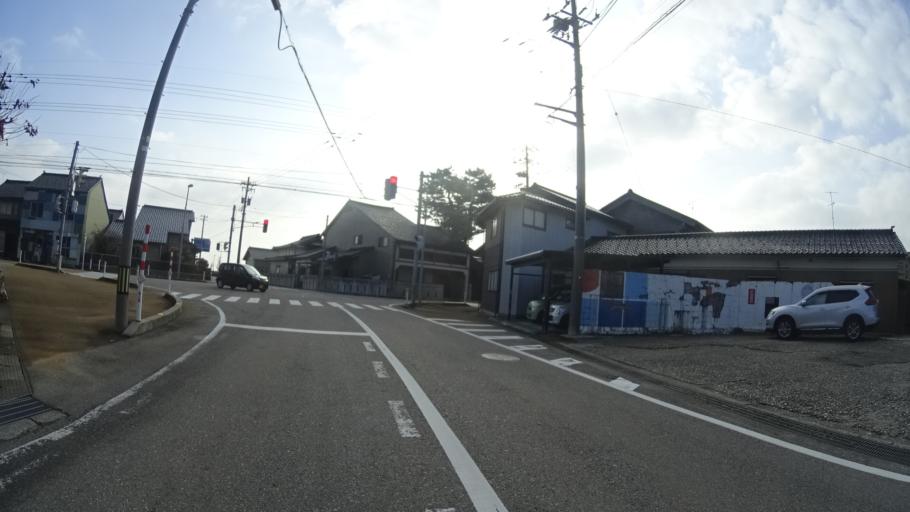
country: JP
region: Toyama
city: Himi
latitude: 36.8719
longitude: 136.9827
